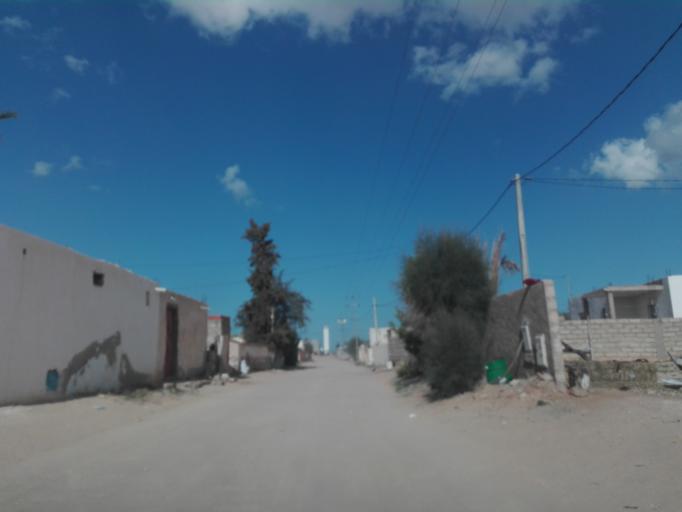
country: TN
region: Madanin
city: Bin Qirdan
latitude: 33.1561
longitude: 11.1939
